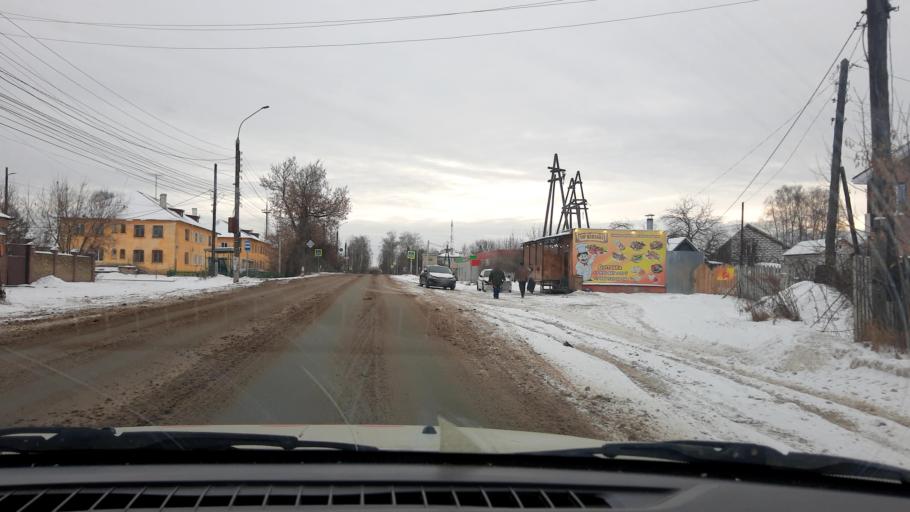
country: RU
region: Nizjnij Novgorod
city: Gorodets
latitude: 56.6572
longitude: 43.4844
